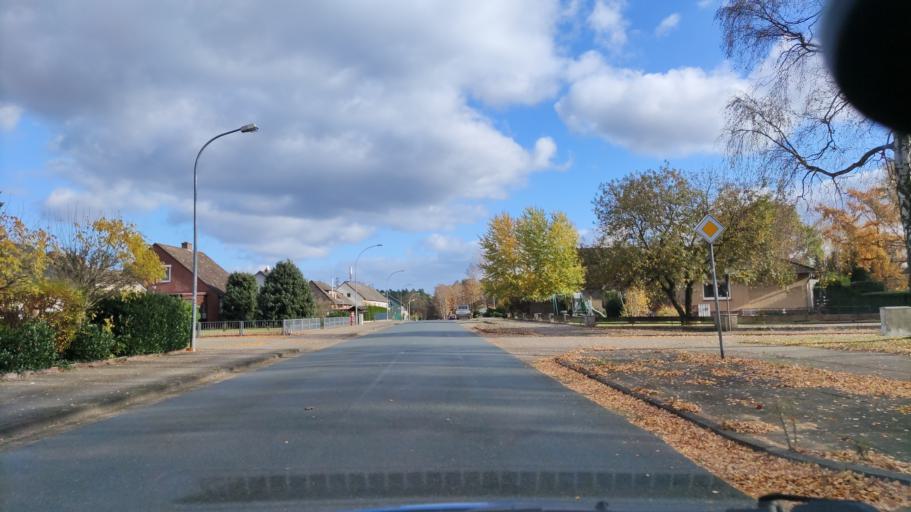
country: DE
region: Lower Saxony
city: Munster
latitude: 53.0021
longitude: 10.1000
